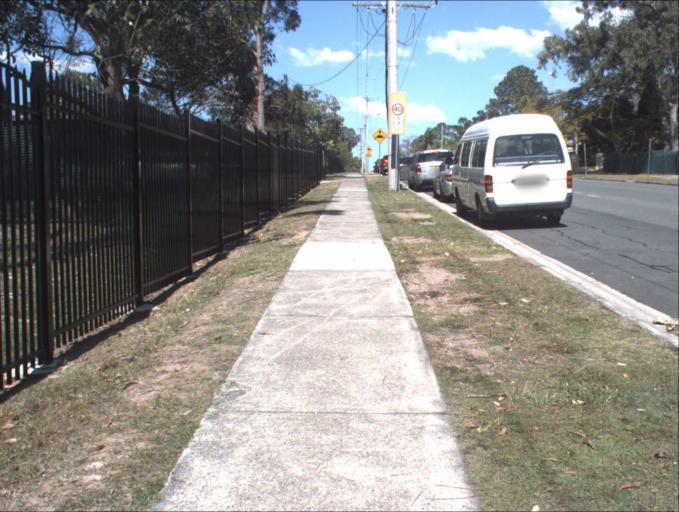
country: AU
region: Queensland
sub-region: Logan
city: Logan City
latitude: -27.6607
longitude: 153.1102
